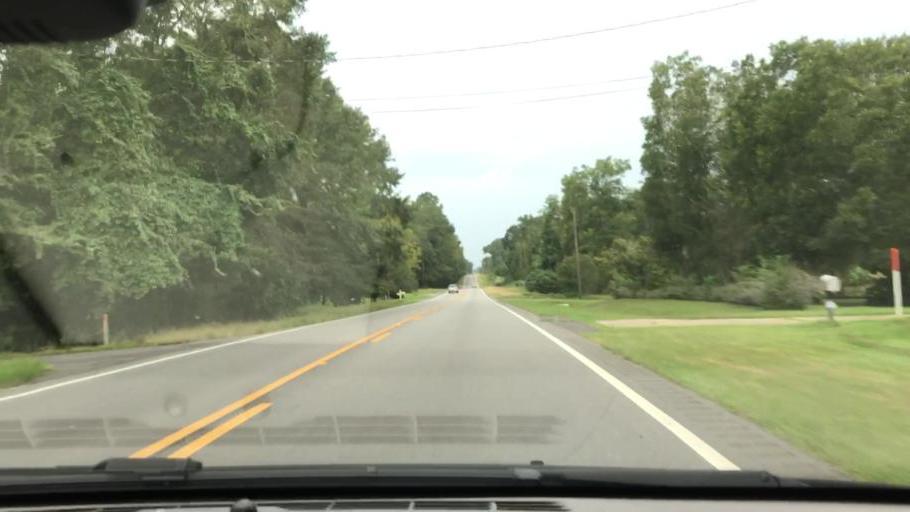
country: US
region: Alabama
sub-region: Houston County
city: Webb
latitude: 31.2739
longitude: -85.1578
